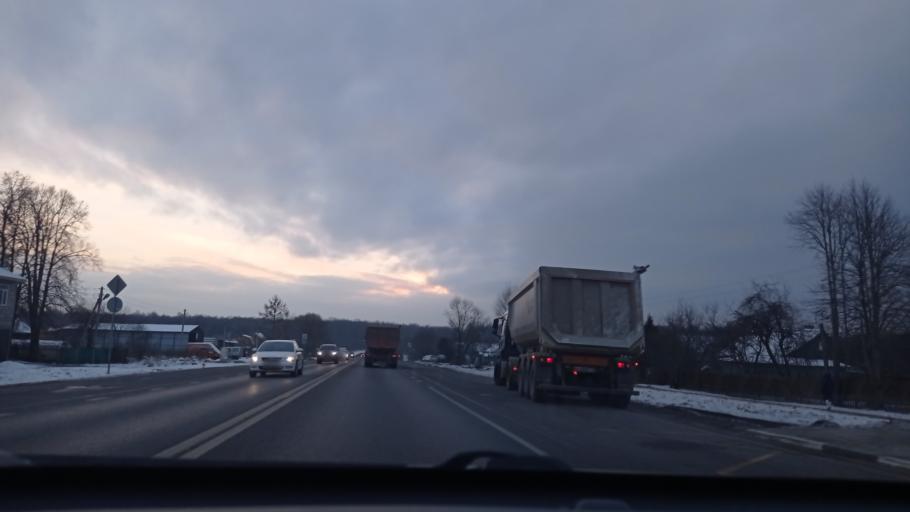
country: RU
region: Moskovskaya
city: Ateptsevo
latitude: 55.1881
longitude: 36.9064
